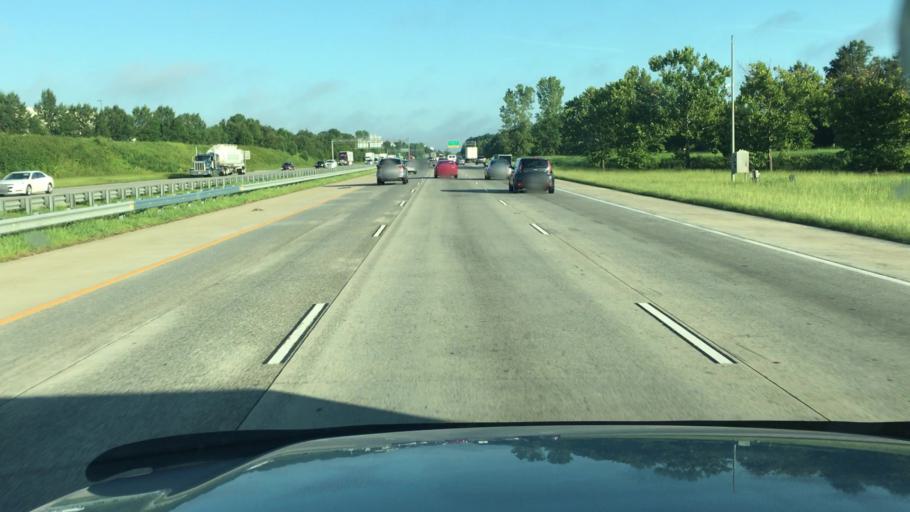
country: US
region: North Carolina
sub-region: Mecklenburg County
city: Pineville
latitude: 35.1432
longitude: -80.9340
